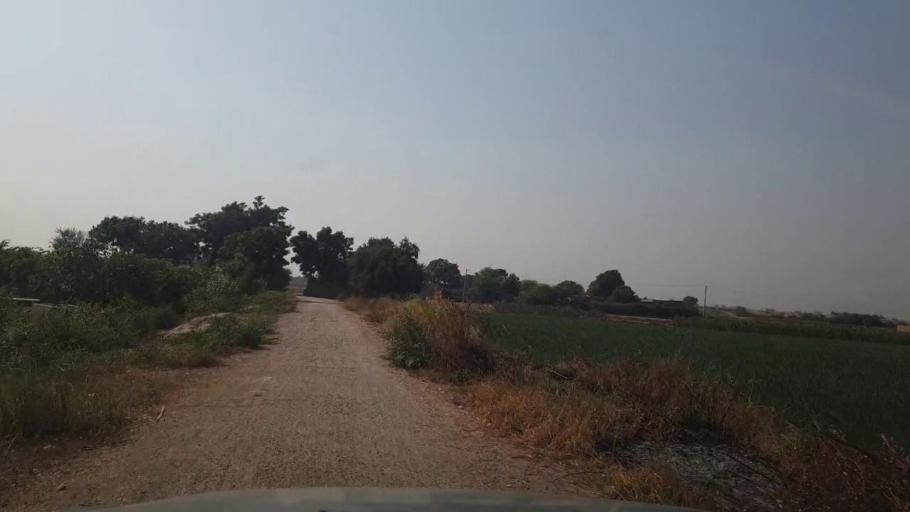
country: PK
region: Sindh
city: Bhit Shah
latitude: 25.7300
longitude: 68.4966
